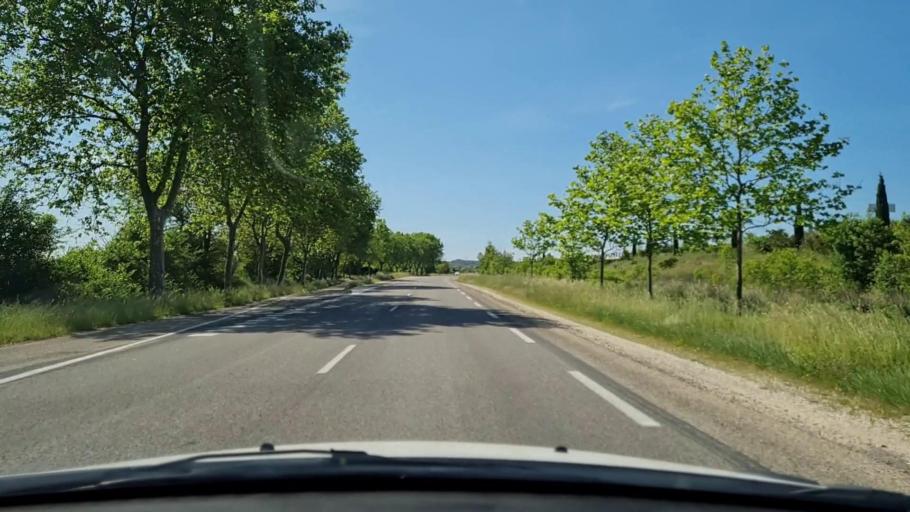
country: FR
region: Languedoc-Roussillon
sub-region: Departement du Gard
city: La Calmette
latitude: 43.9447
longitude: 4.2513
